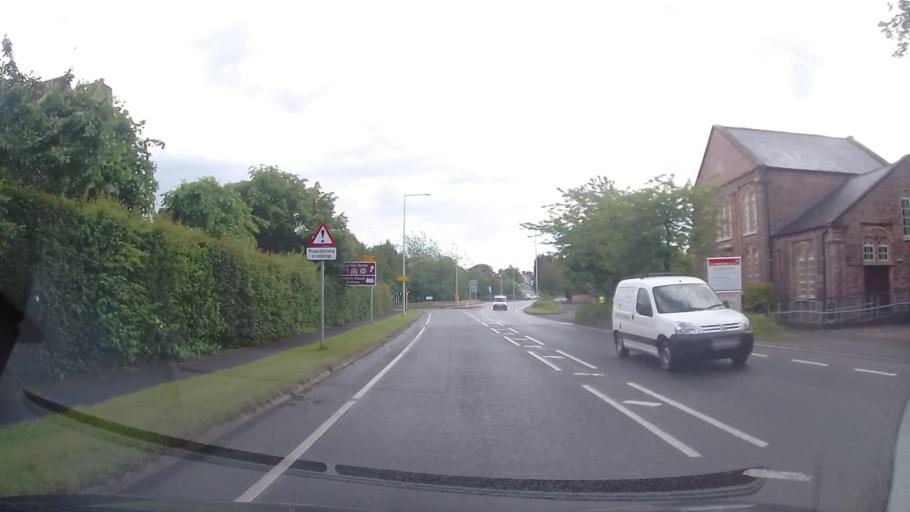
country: GB
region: England
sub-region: Telford and Wrekin
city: Ironbridge
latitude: 52.6621
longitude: -2.4895
